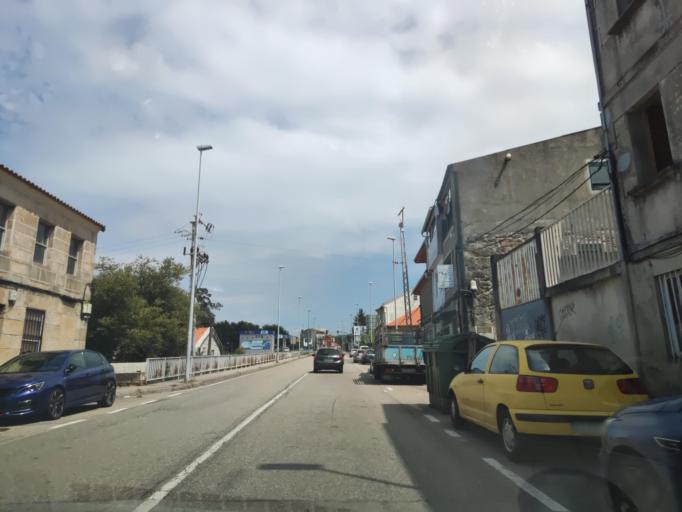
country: ES
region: Galicia
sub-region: Provincia de Pontevedra
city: Vigo
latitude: 42.2539
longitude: -8.6861
